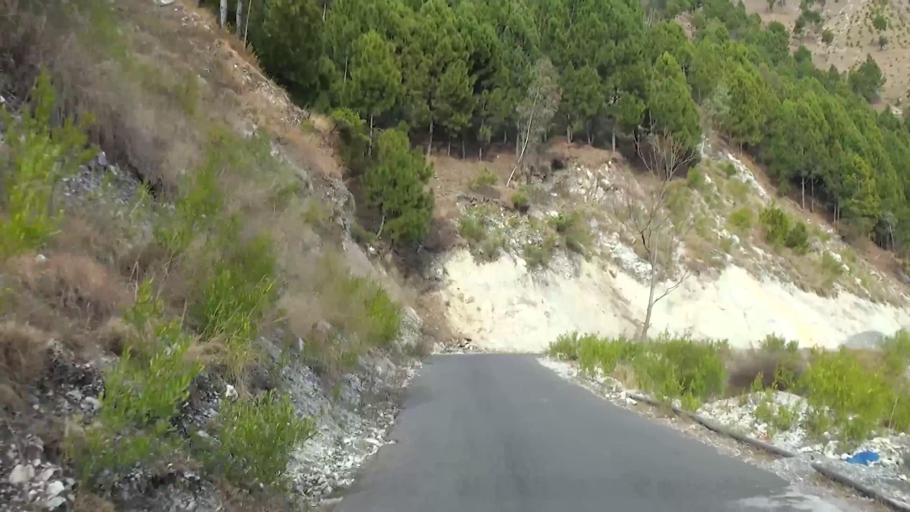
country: PK
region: Azad Kashmir
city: Muzaffarabad
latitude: 34.3667
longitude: 73.5020
